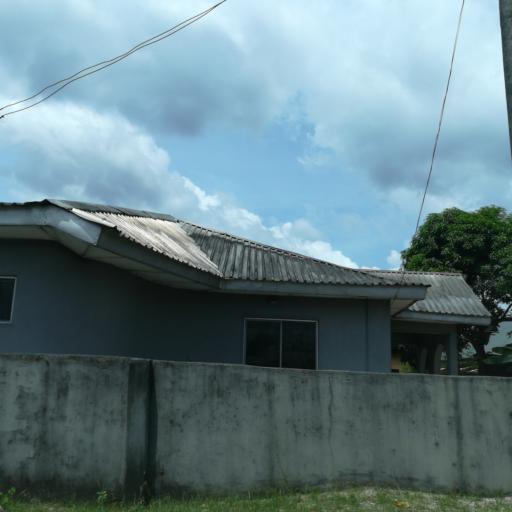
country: NG
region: Rivers
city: Okrika
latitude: 4.7759
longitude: 7.0604
